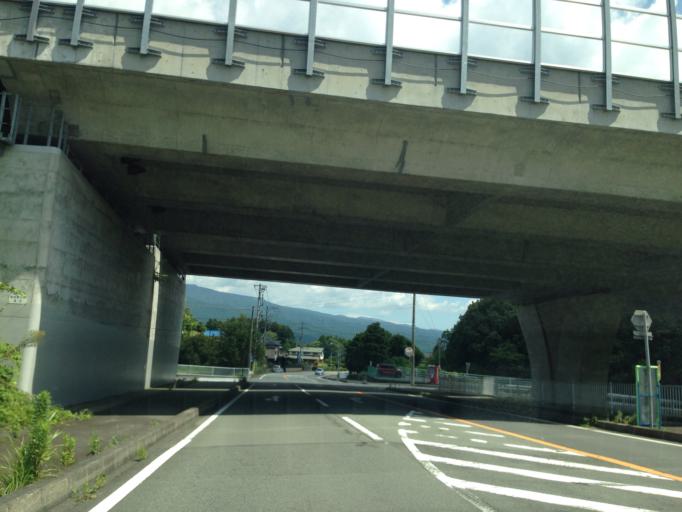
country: JP
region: Shizuoka
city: Gotemba
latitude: 35.2217
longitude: 138.8881
